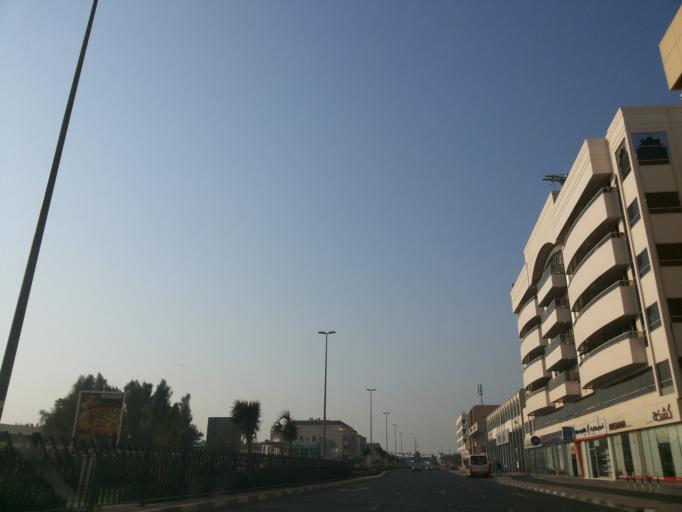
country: AE
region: Ash Shariqah
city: Sharjah
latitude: 25.2783
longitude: 55.3457
